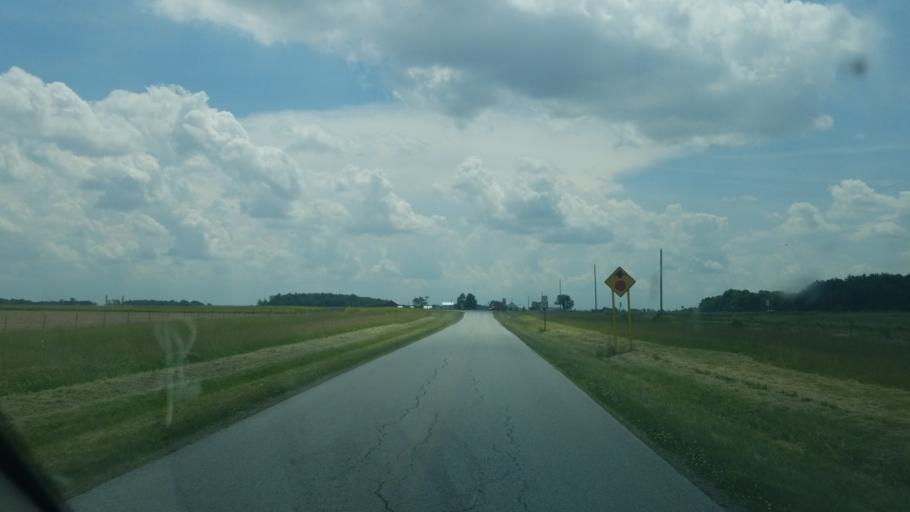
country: US
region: Ohio
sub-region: Hancock County
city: Arlington
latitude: 40.8298
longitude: -83.6000
